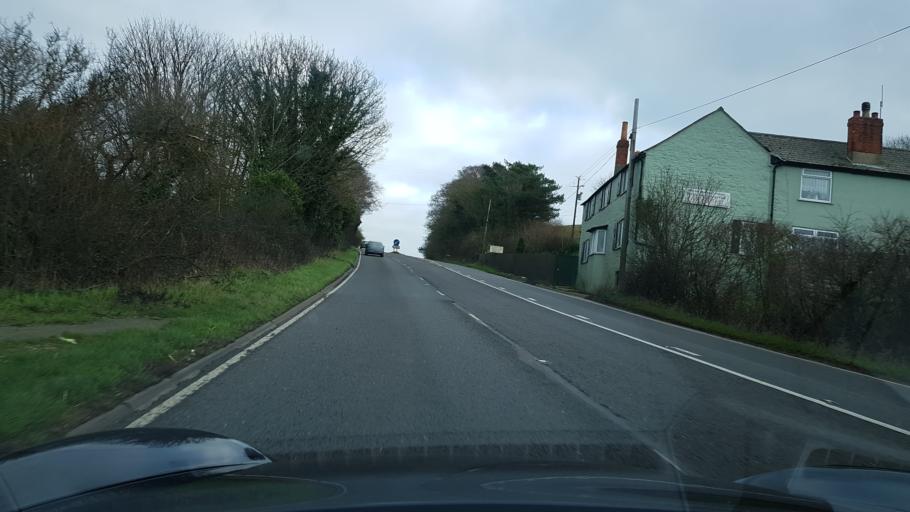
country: GB
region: England
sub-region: Dorset
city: Bridport
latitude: 50.7313
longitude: -2.6875
